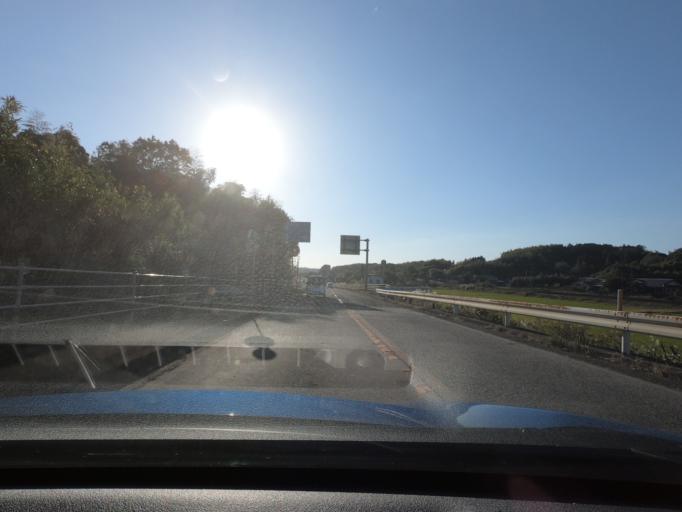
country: JP
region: Kagoshima
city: Akune
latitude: 32.0705
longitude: 130.2433
